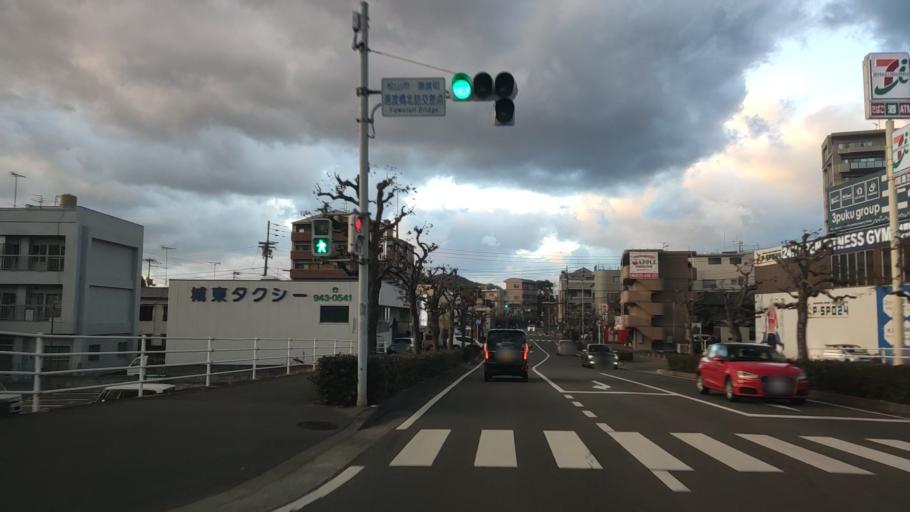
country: JP
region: Ehime
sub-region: Shikoku-chuo Shi
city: Matsuyama
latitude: 33.8403
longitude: 132.7854
